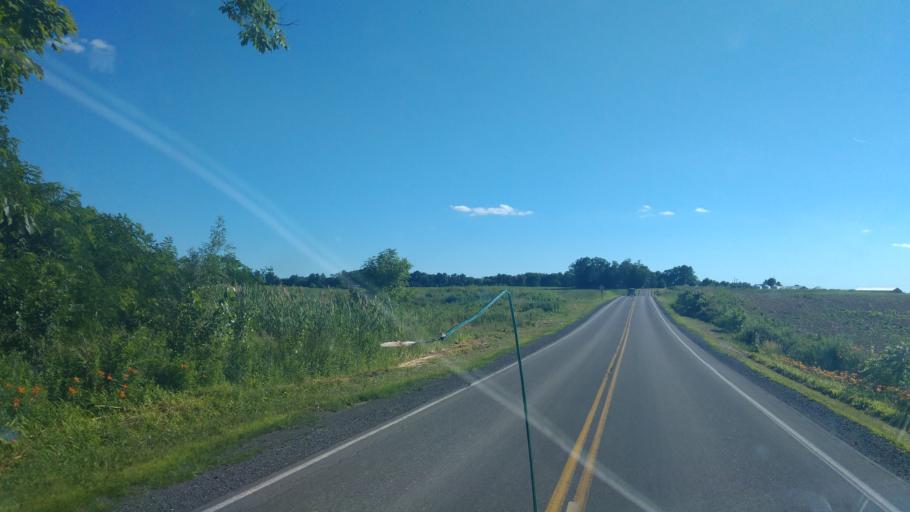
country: US
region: New York
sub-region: Wayne County
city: Clyde
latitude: 43.0004
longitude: -76.9032
